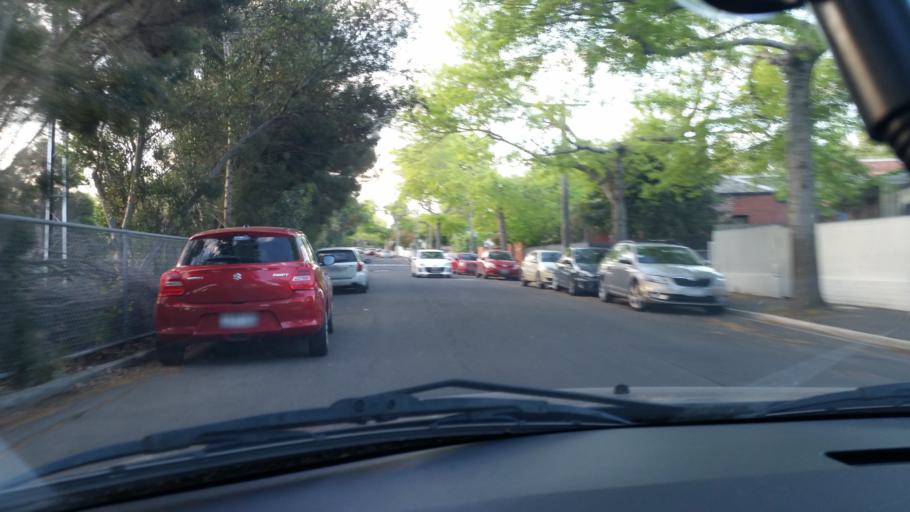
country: AU
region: Victoria
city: Kensington
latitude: -37.7830
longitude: 144.9280
